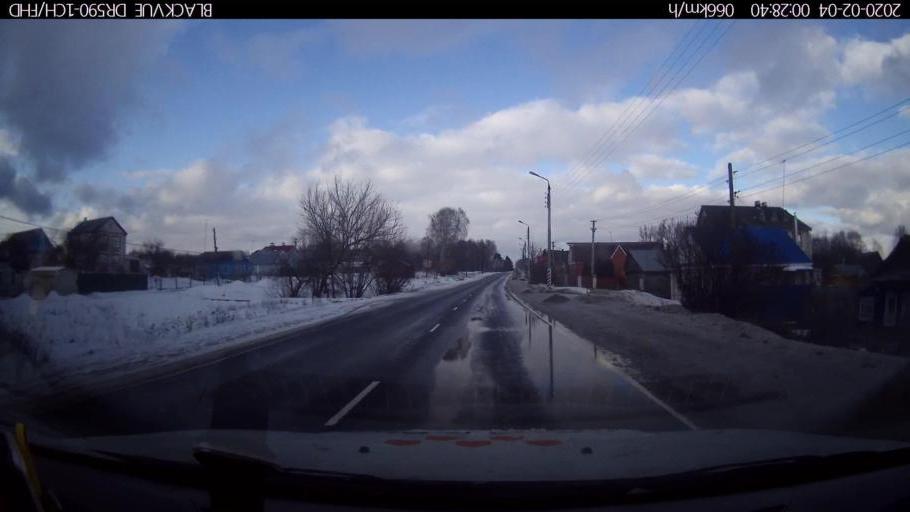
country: RU
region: Nizjnij Novgorod
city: Kstovo
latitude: 56.0231
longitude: 44.1691
